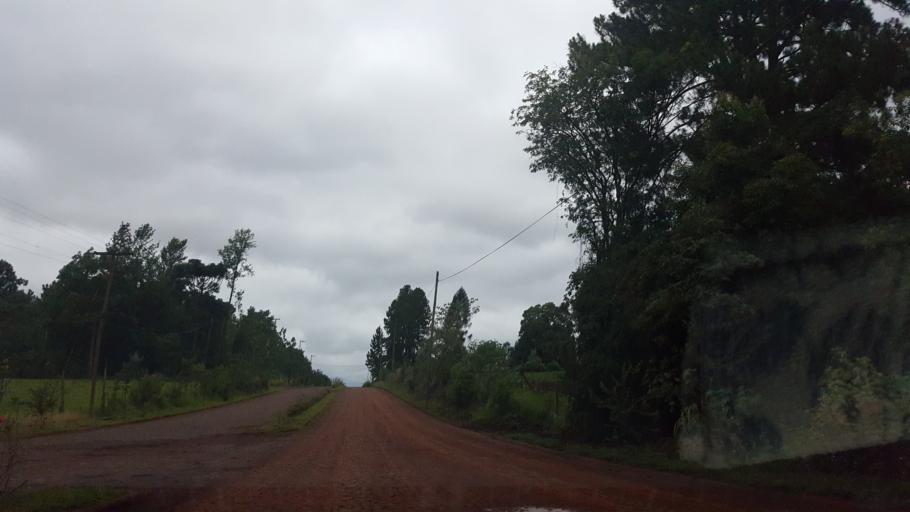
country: AR
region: Misiones
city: Ruiz de Montoya
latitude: -26.9630
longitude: -55.0567
